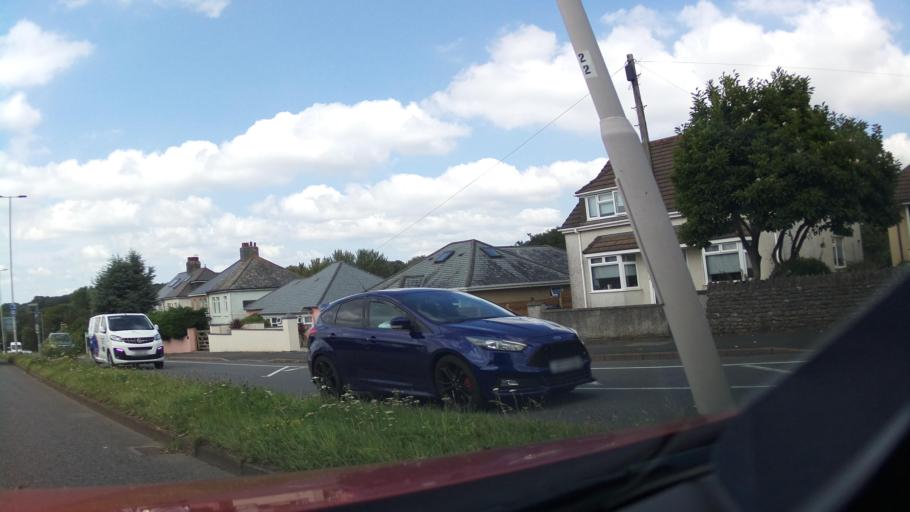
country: GB
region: England
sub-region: Plymouth
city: Plymstock
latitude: 50.3640
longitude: -4.0769
